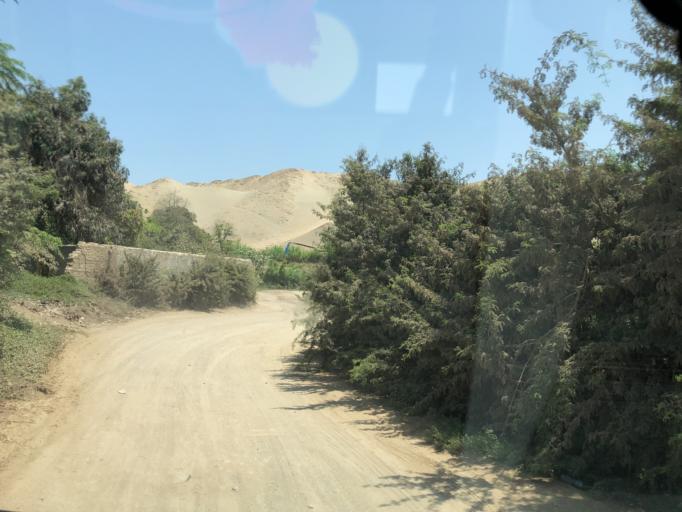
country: PE
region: Lima
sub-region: Provincia de Canete
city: Quilmana
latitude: -13.0044
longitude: -76.4536
